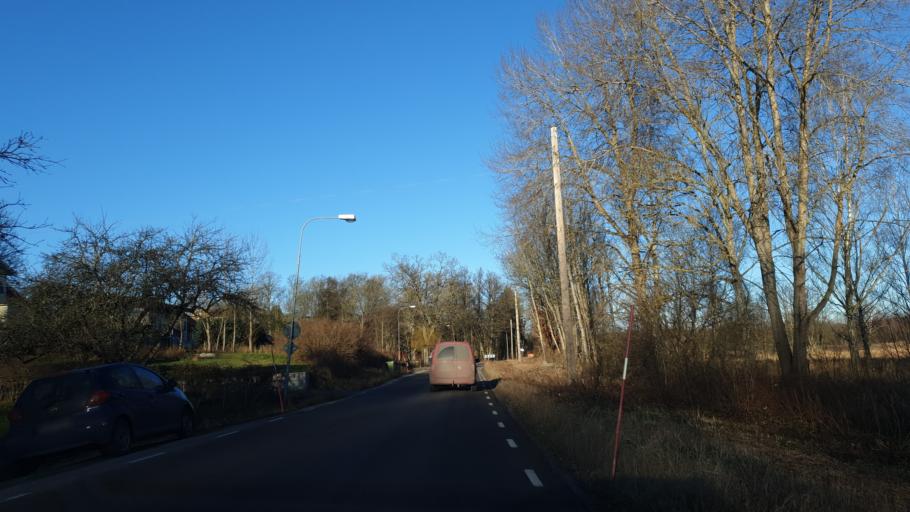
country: SE
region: Blekinge
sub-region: Karlskrona Kommun
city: Nattraby
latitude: 56.2635
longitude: 15.5088
